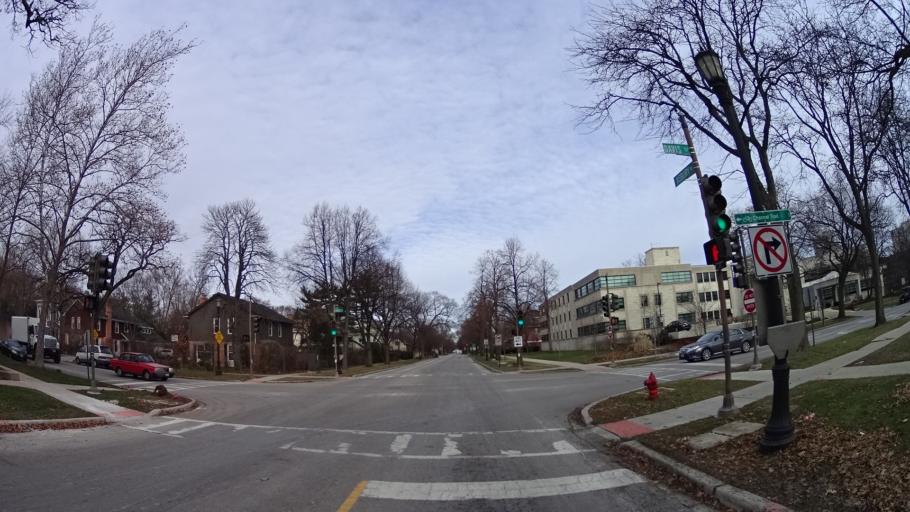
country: US
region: Illinois
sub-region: Cook County
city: Evanston
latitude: 42.0469
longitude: -87.6901
